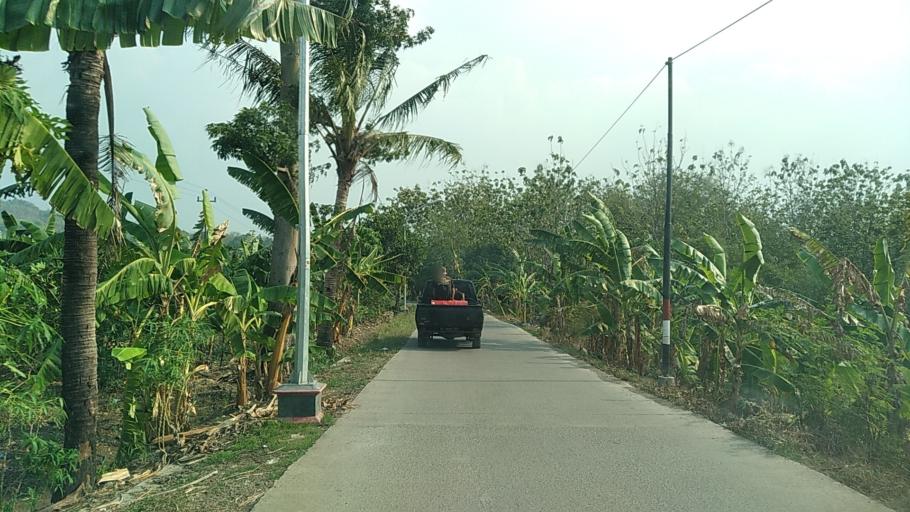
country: ID
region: Central Java
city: Mranggen
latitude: -7.0741
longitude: 110.4680
